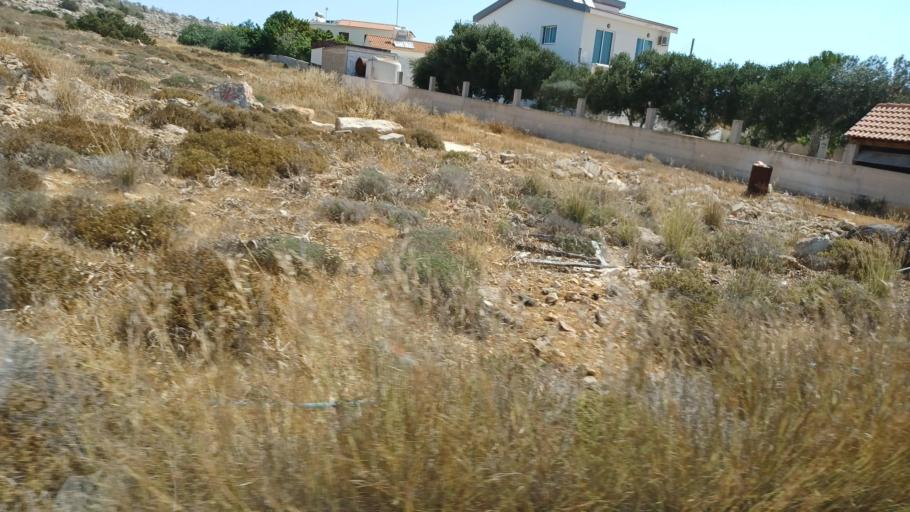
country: CY
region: Ammochostos
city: Paralimni
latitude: 35.0060
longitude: 33.9706
